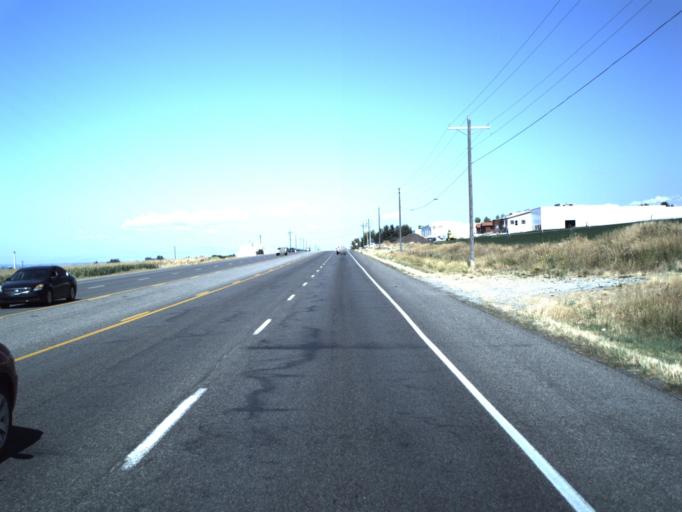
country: US
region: Utah
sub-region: Cache County
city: Richmond
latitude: 41.9028
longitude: -111.8147
